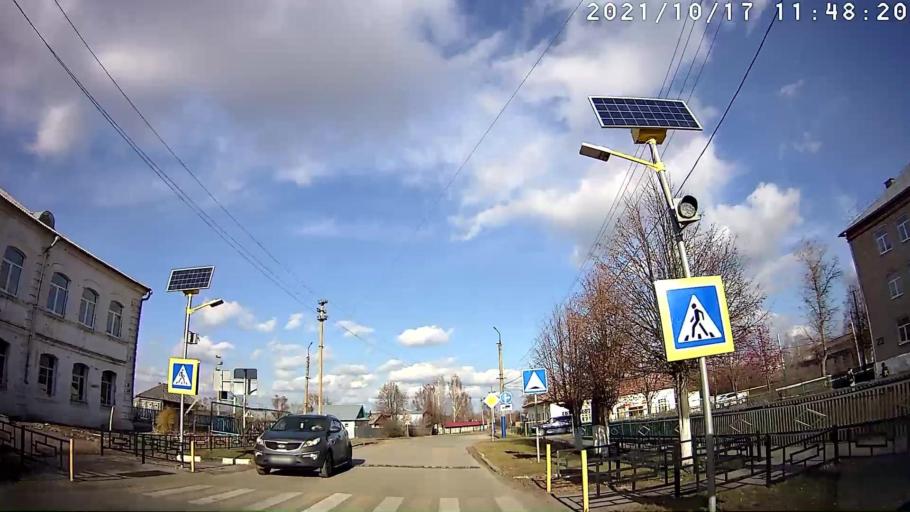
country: RU
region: Mariy-El
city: Kuzhener
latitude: 57.0030
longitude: 48.7339
